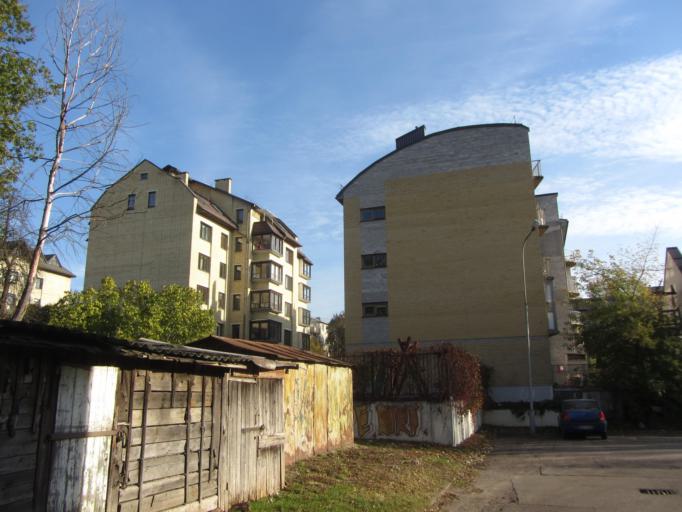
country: LT
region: Vilnius County
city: Vilkpede
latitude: 54.6752
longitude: 25.2457
